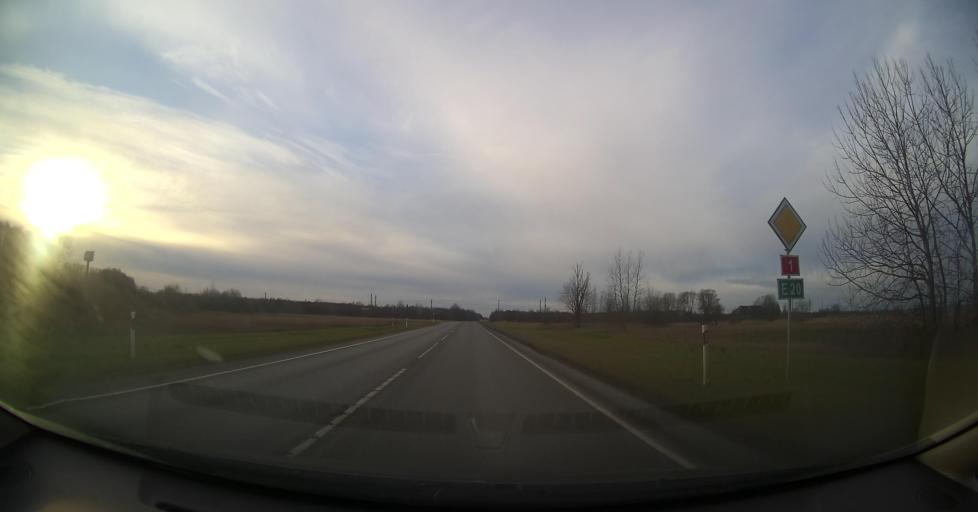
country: EE
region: Ida-Virumaa
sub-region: Sillamaee linn
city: Sillamae
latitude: 59.3897
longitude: 27.7343
